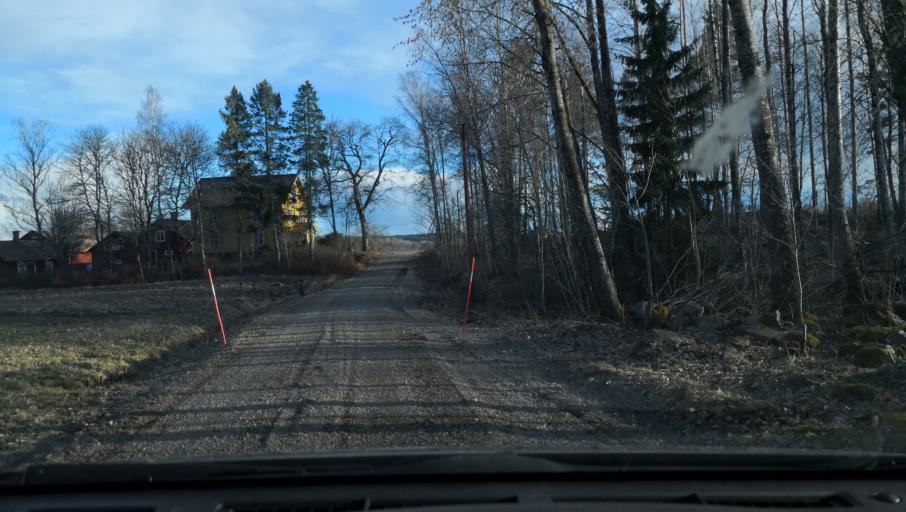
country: SE
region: Vaestmanland
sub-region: Arboga Kommun
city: Arboga
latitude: 59.4267
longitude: 15.7507
